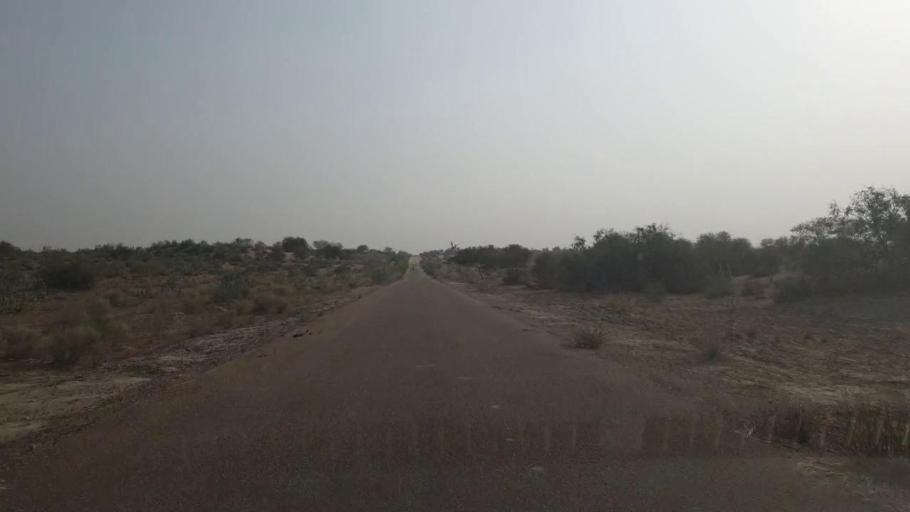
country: PK
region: Sindh
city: Chor
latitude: 25.4636
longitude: 69.9670
